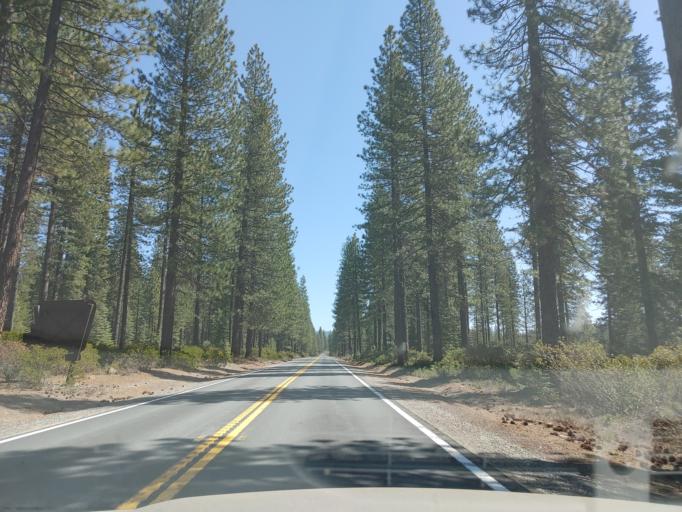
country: US
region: California
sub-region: Siskiyou County
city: McCloud
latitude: 41.2664
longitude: -121.8679
